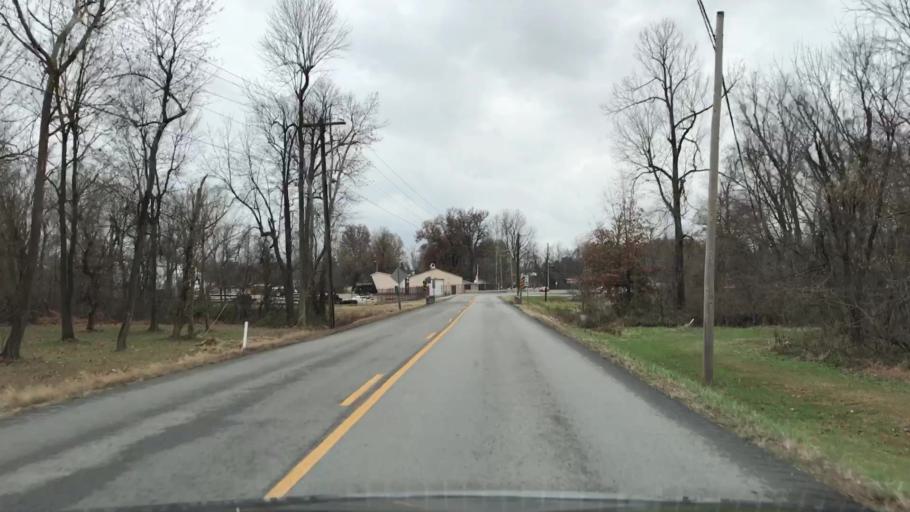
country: US
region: Kentucky
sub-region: McLean County
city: Calhoun
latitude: 37.5476
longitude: -87.2557
